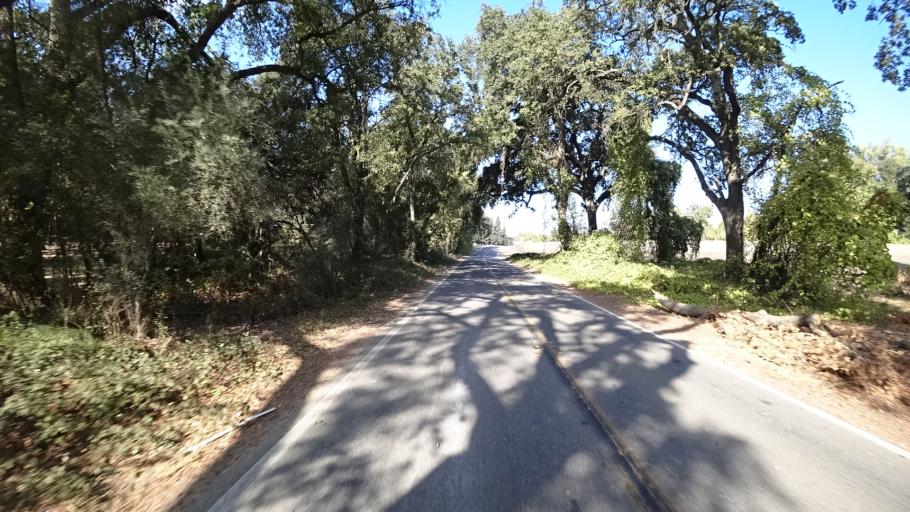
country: US
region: California
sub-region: Yolo County
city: Woodland
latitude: 38.8550
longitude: -121.7846
